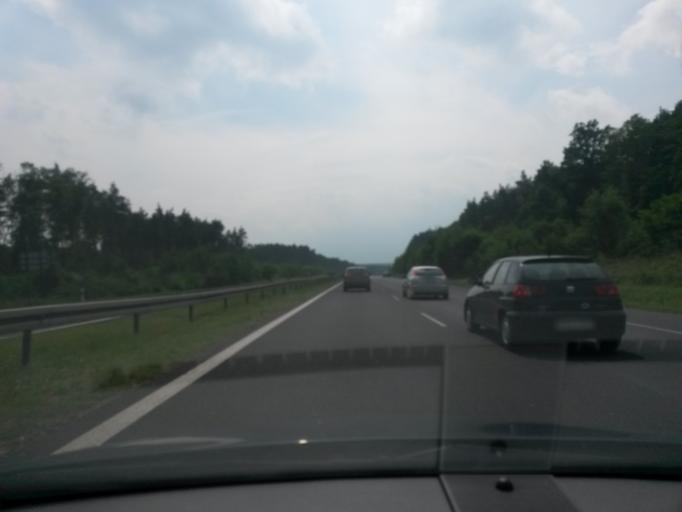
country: PL
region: Lodz Voivodeship
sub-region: Powiat radomszczanski
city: Gomunice
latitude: 51.1693
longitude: 19.4612
